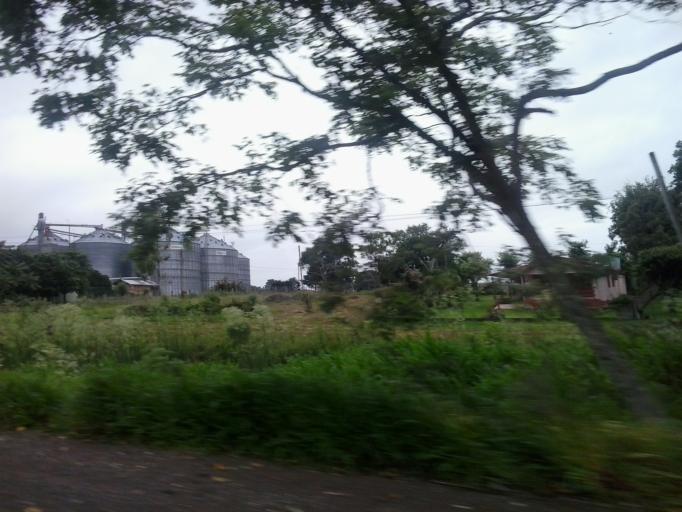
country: BR
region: Rio Grande do Sul
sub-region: Santa Maria
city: Santa Maria
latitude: -29.7222
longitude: -53.3760
